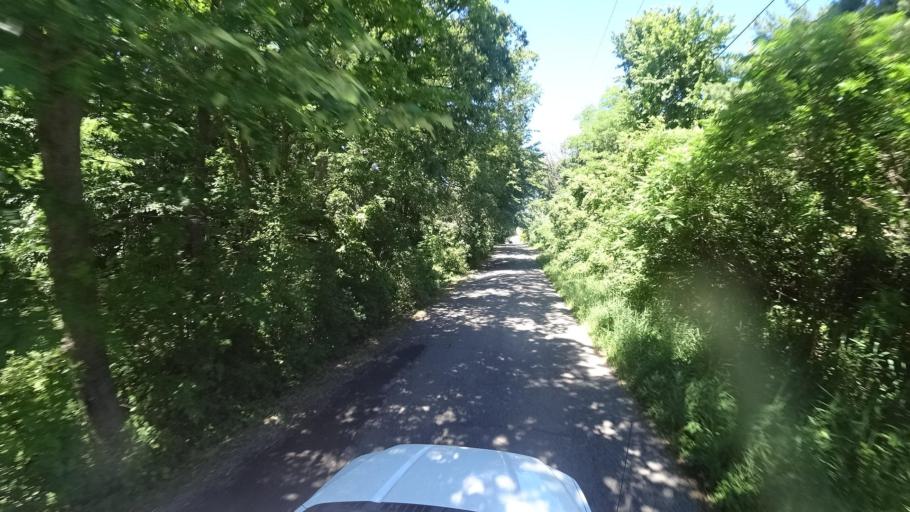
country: US
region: Indiana
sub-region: Porter County
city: Porter
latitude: 41.6336
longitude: -87.0868
